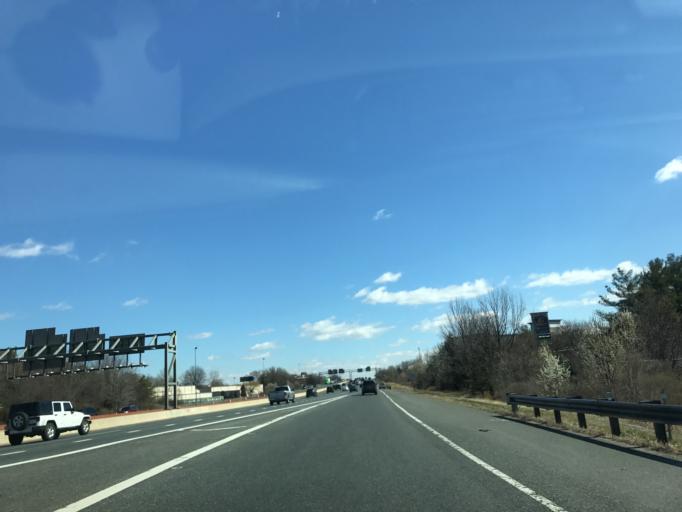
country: US
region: Maryland
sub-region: Anne Arundel County
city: Parole
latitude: 38.9825
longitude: -76.5507
